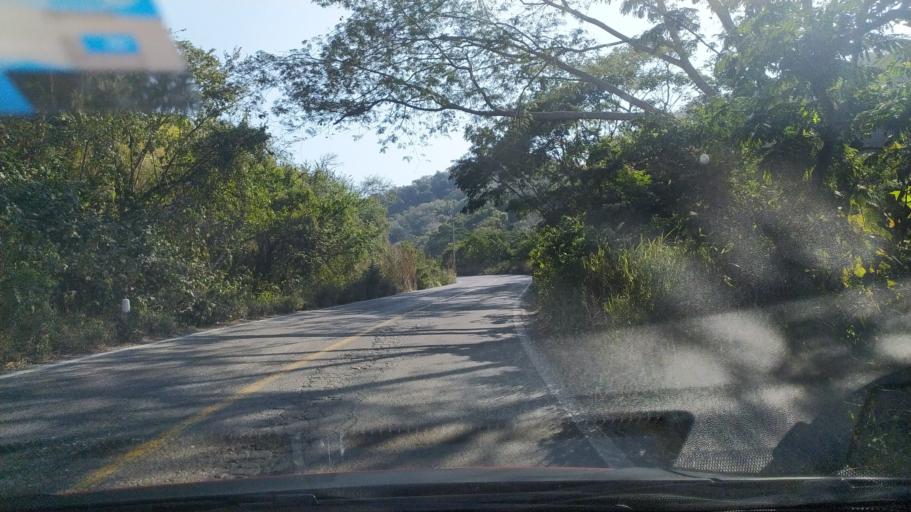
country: MX
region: Michoacan
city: Coahuayana Viejo
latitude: 18.6165
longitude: -103.6780
